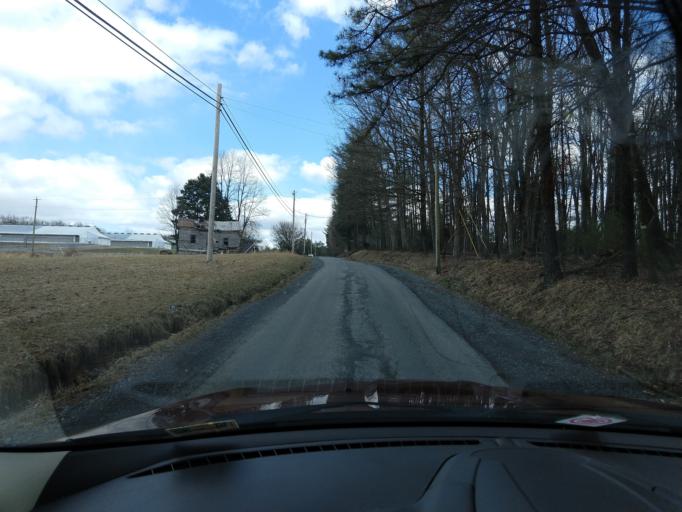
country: US
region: West Virginia
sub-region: Greenbrier County
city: Fairlea
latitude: 37.8279
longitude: -80.5314
